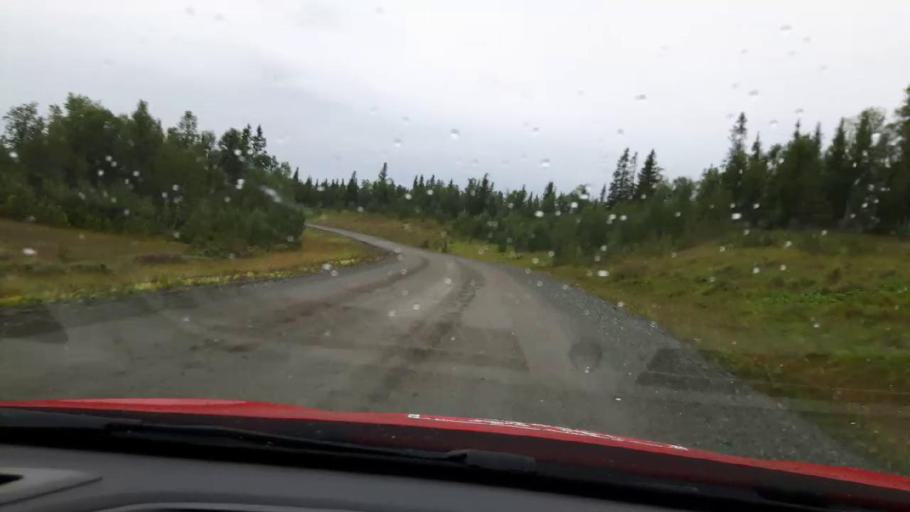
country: NO
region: Nord-Trondelag
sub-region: Meraker
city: Meraker
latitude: 63.5654
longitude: 12.2873
